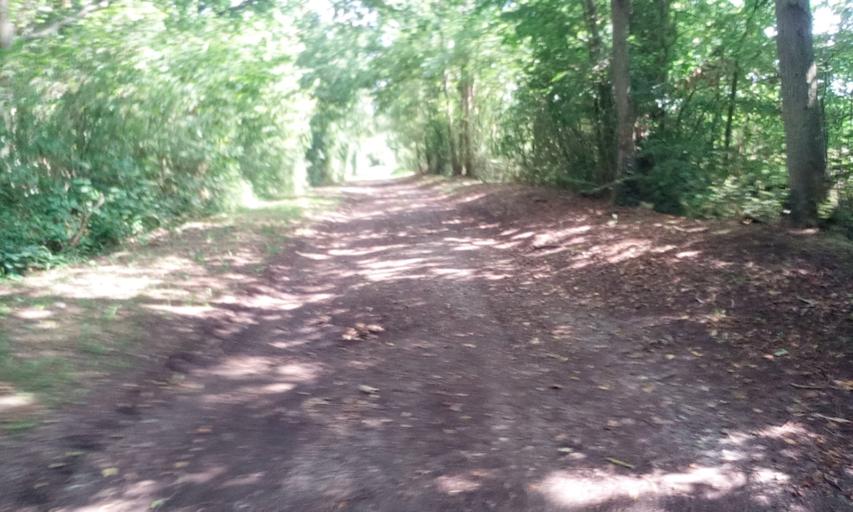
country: FR
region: Lower Normandy
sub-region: Departement du Calvados
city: Argences
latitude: 49.1457
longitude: -0.1520
